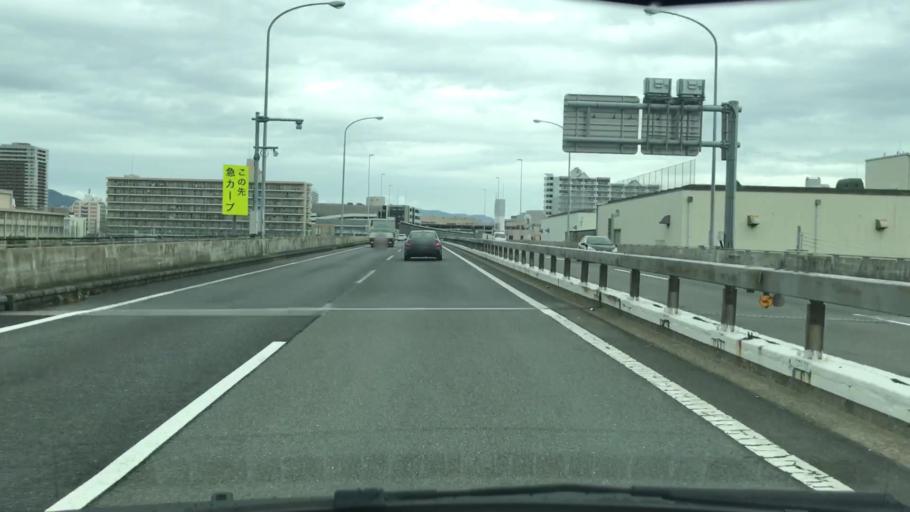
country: JP
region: Hyogo
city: Nishinomiya-hama
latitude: 34.7370
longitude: 135.3595
